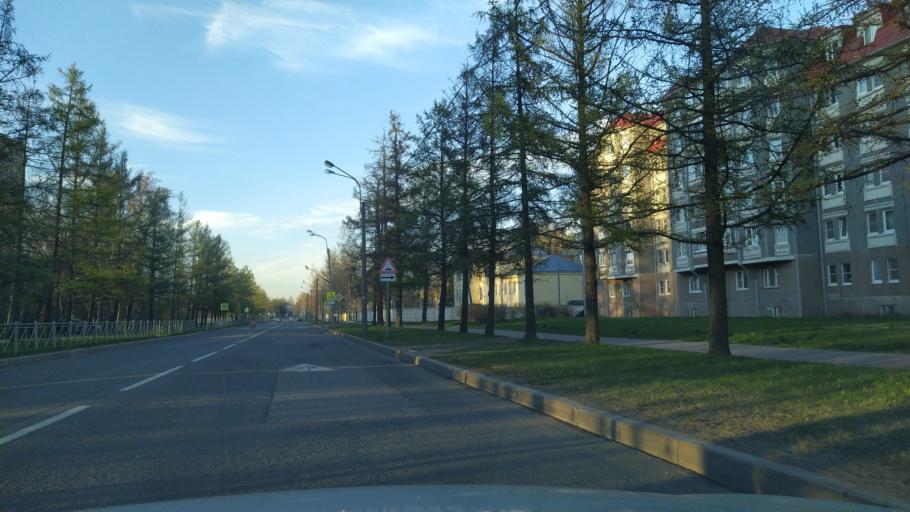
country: RU
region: St.-Petersburg
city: Pushkin
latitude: 59.7043
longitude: 30.3731
